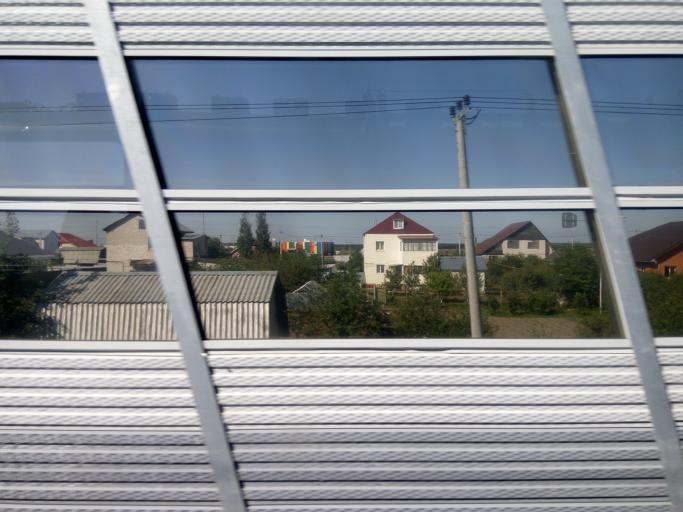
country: RU
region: Tatarstan
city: Stolbishchi
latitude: 55.6626
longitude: 49.2215
